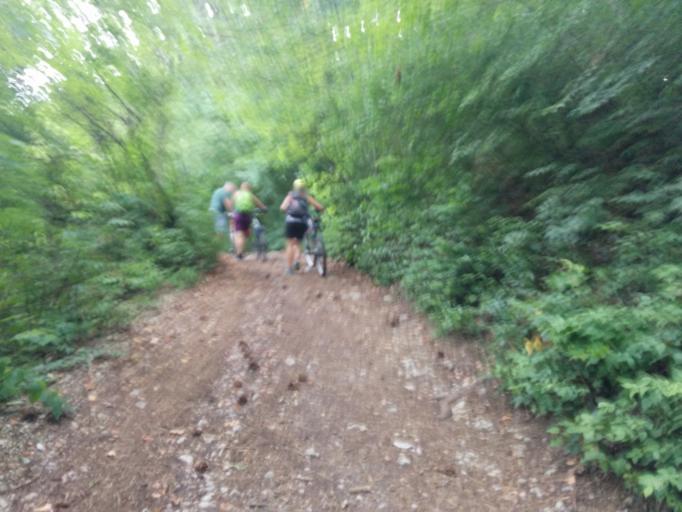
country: AT
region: Lower Austria
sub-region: Politischer Bezirk Modling
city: Gumpoldskirchen
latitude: 48.0424
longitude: 16.2573
